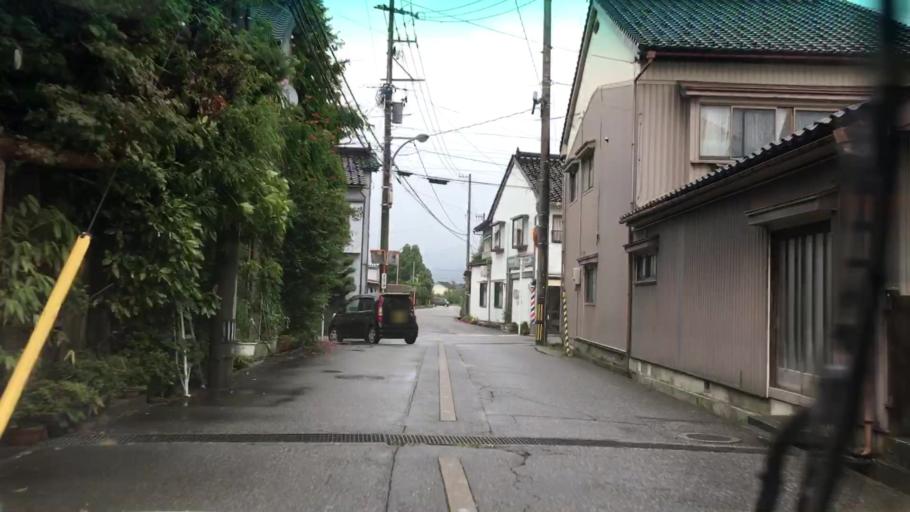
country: JP
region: Toyama
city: Kamiichi
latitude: 36.6620
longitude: 137.3171
